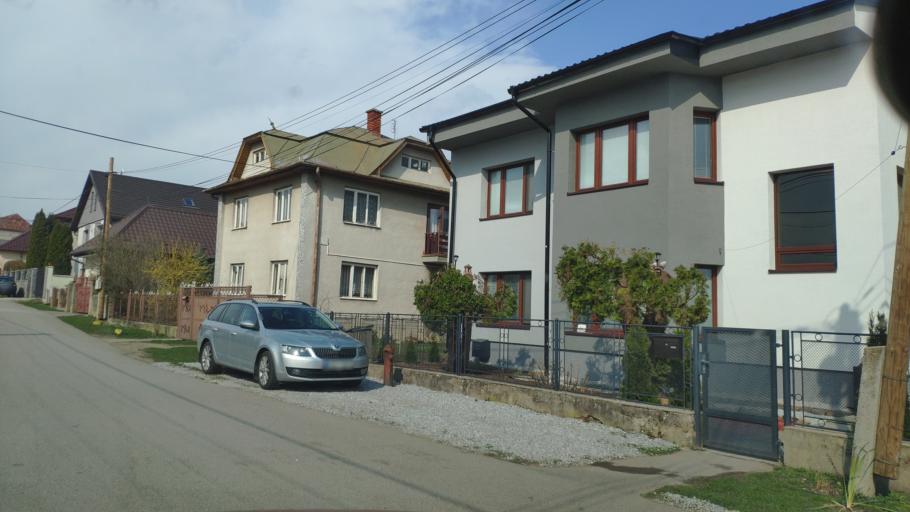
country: SK
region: Kosicky
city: Kosice
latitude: 48.6217
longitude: 21.3689
